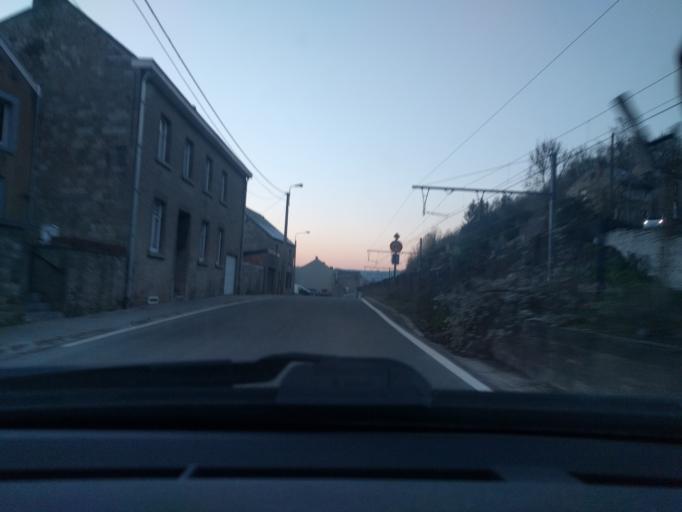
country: BE
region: Wallonia
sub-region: Province de Namur
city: Noville-les-Bois
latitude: 50.4704
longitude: 4.9893
